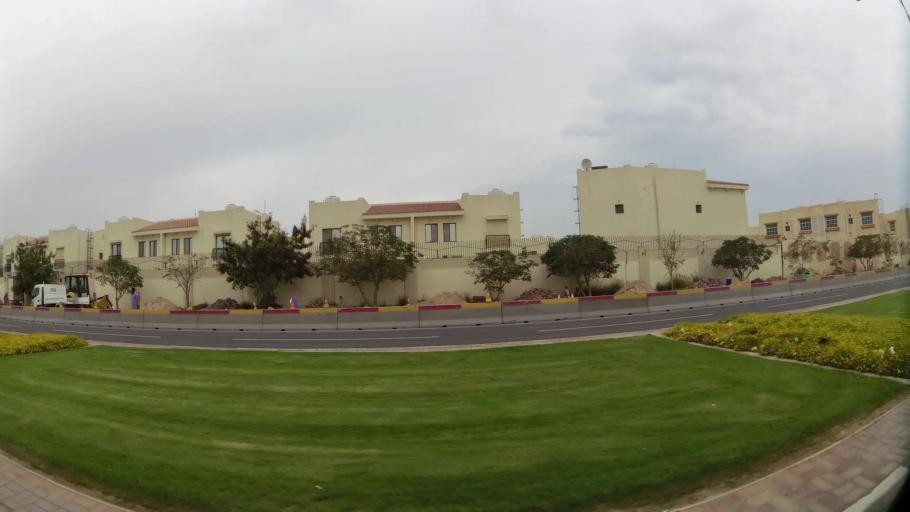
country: QA
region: Baladiyat ad Dawhah
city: Doha
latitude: 25.3275
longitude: 51.4845
